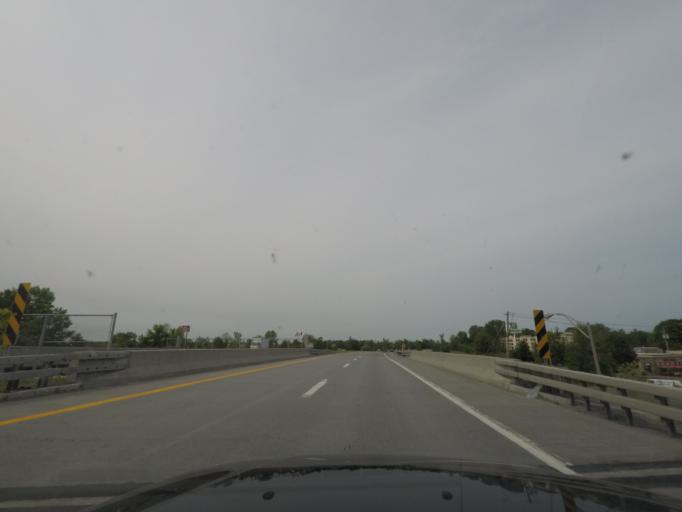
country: US
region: New York
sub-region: Clinton County
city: Plattsburgh West
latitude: 44.6964
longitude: -73.4901
